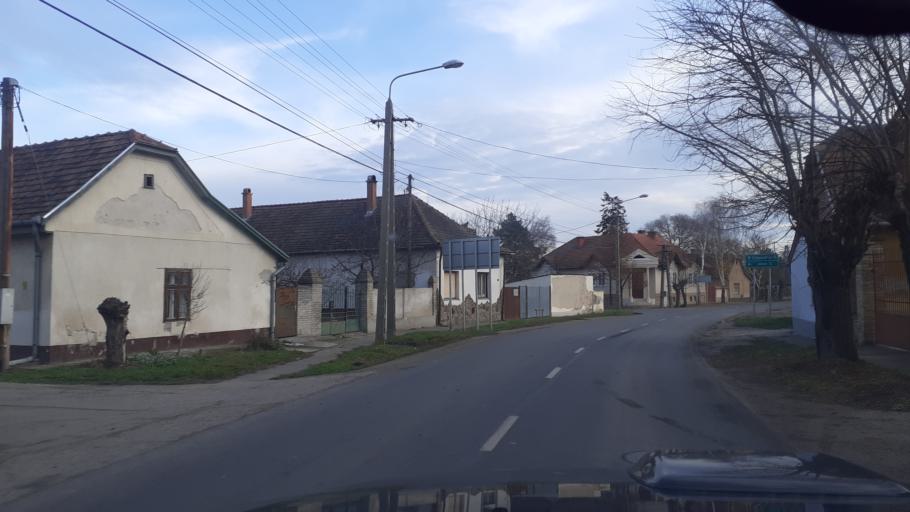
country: HU
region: Bacs-Kiskun
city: Szabadszallas
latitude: 46.8737
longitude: 19.2233
